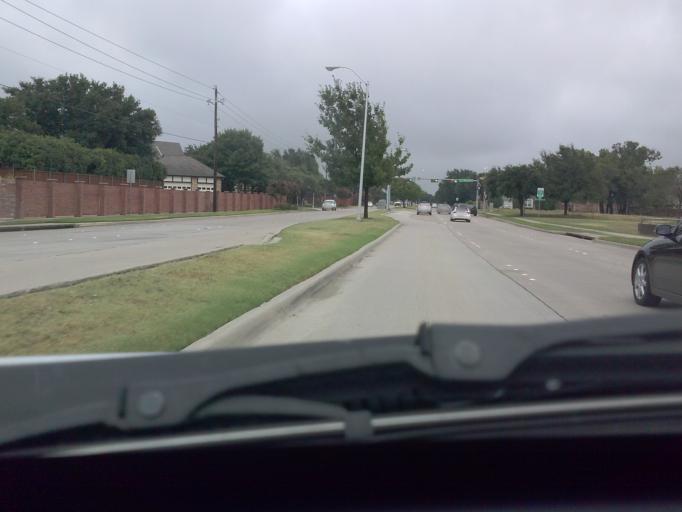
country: US
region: Texas
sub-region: Collin County
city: Plano
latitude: 33.0717
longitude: -96.7604
